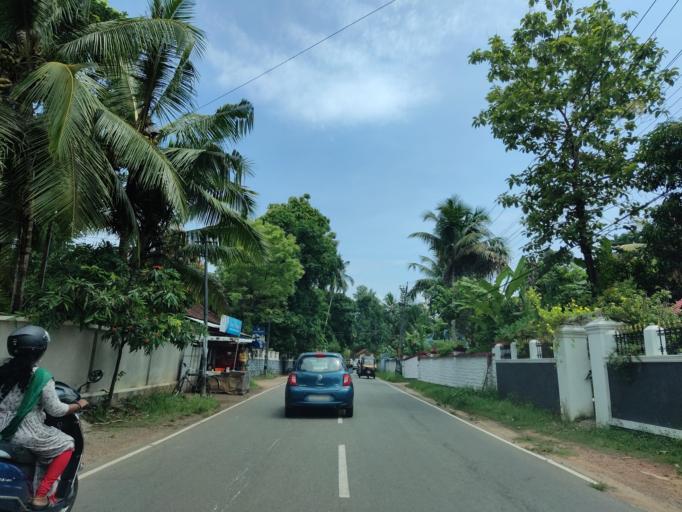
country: IN
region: Kerala
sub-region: Alappuzha
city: Chengannur
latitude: 9.3126
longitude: 76.6044
